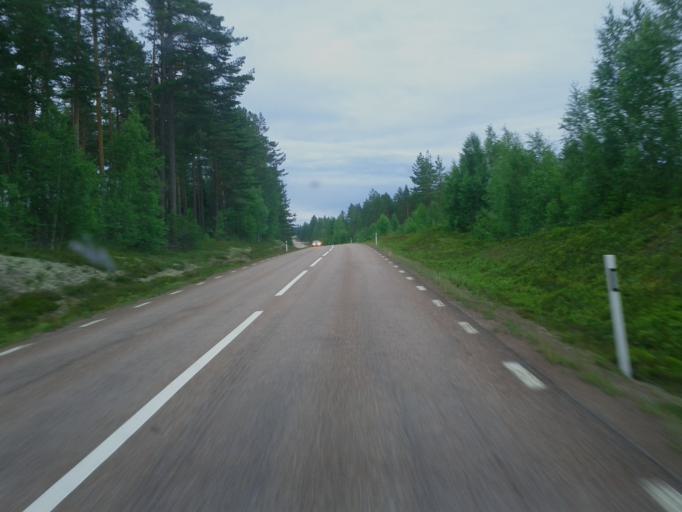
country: SE
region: Dalarna
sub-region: Mora Kommun
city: Mora
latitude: 61.0743
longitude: 14.3548
